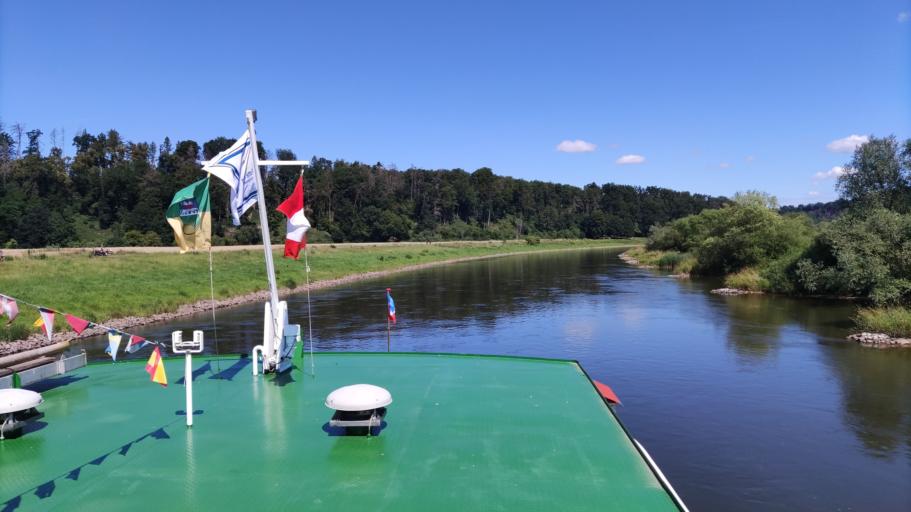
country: DE
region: Lower Saxony
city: Furstenberg
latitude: 51.7192
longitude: 9.3873
